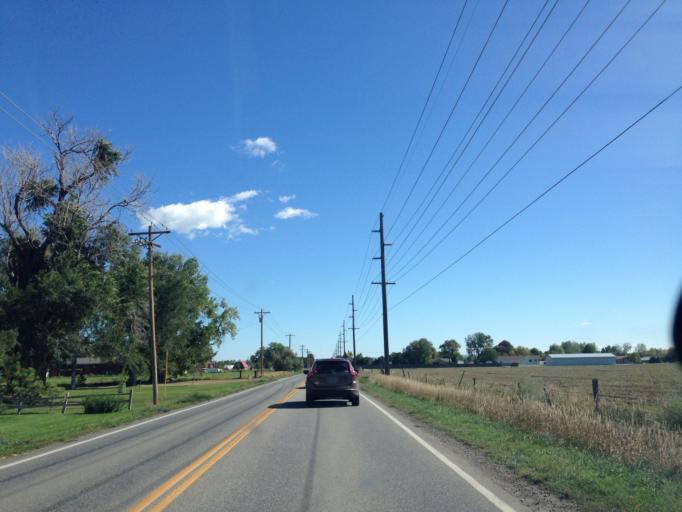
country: US
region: Montana
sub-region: Yellowstone County
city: Billings
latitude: 45.7841
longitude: -108.6437
